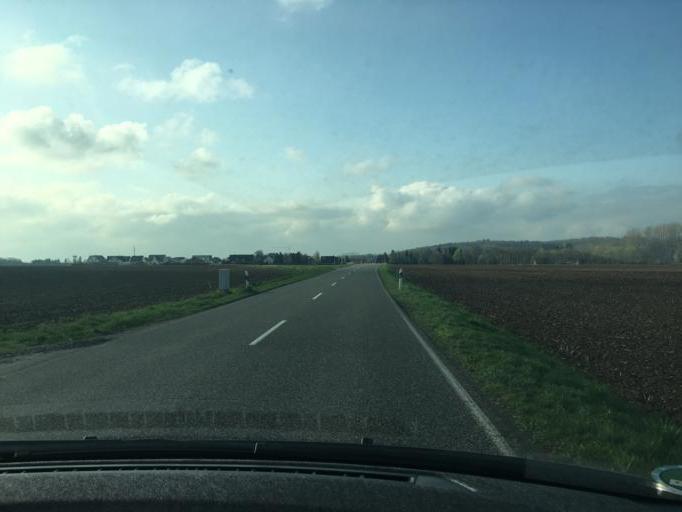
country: DE
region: North Rhine-Westphalia
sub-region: Regierungsbezirk Koln
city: Weilerswist
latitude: 50.7283
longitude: 6.8985
